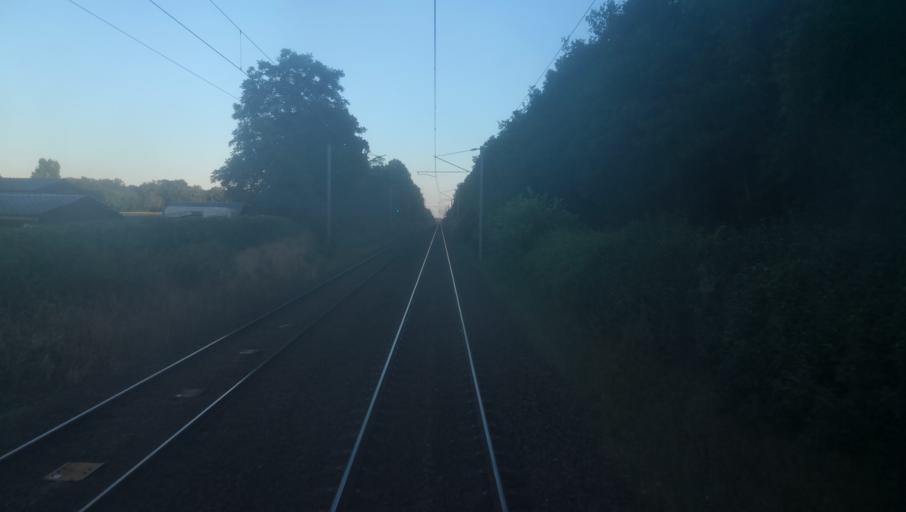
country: FR
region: Bourgogne
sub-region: Departement de la Nievre
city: La Charite-sur-Loire
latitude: 47.2217
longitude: 3.0168
